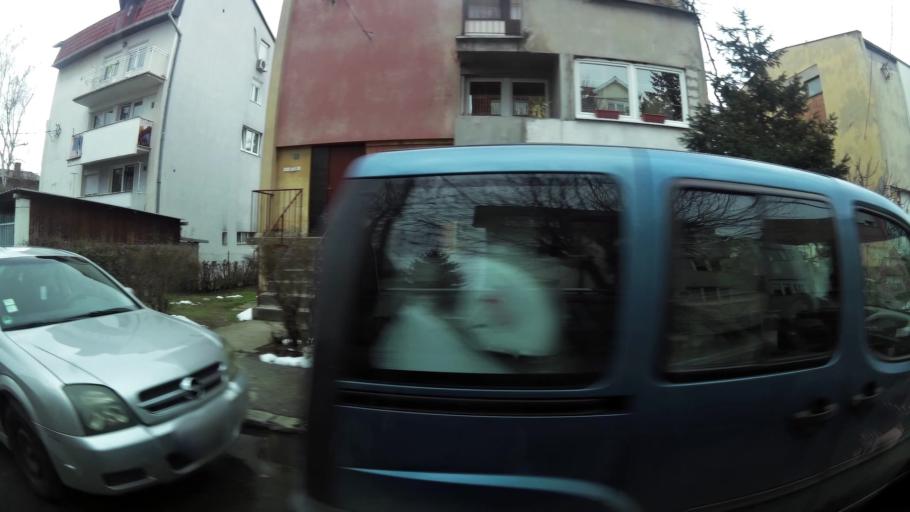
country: RS
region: Central Serbia
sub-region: Belgrade
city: Rakovica
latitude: 44.7506
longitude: 20.4099
